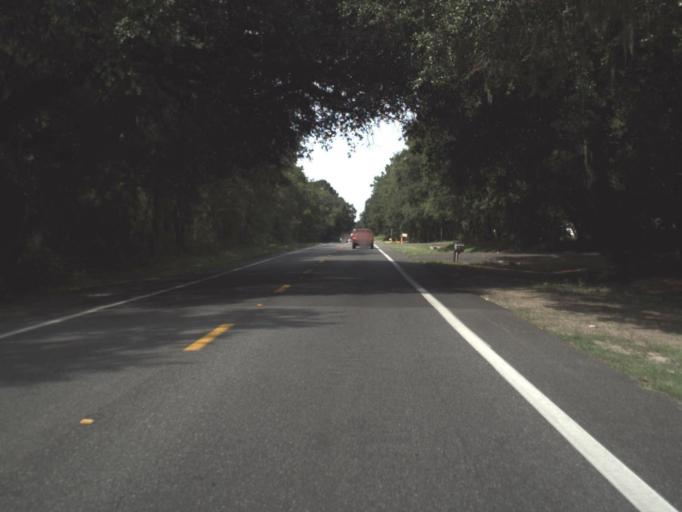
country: US
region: Florida
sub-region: Suwannee County
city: Live Oak
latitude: 30.2673
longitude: -83.0225
